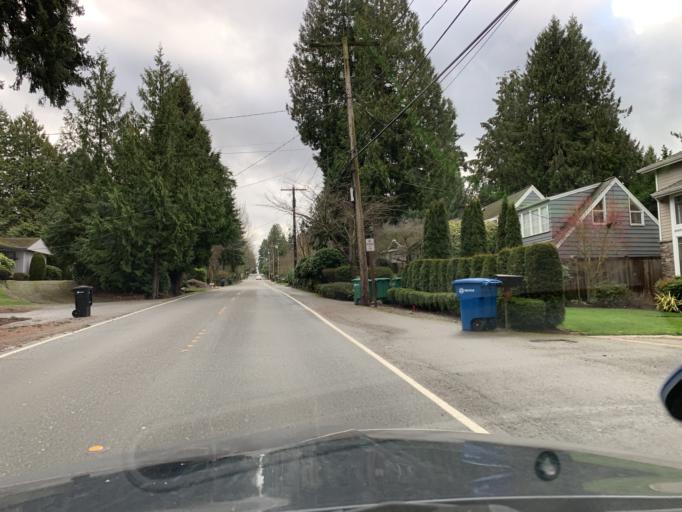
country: US
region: Washington
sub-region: King County
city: Mercer Island
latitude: 47.5885
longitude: -122.2431
